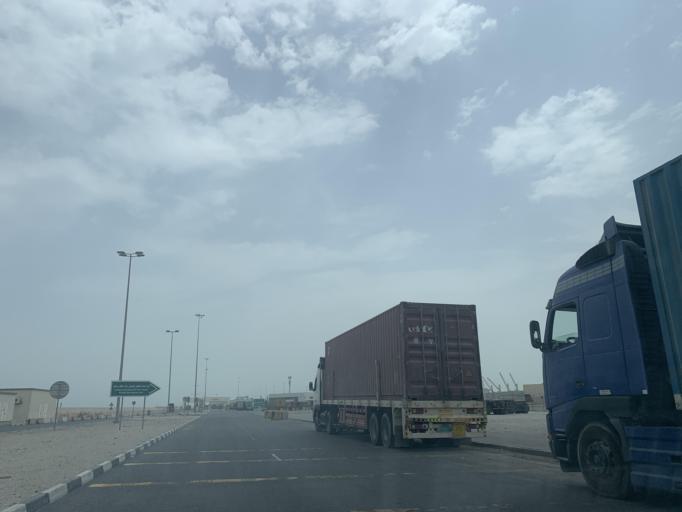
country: BH
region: Muharraq
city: Al Hadd
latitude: 26.1993
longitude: 50.7105
